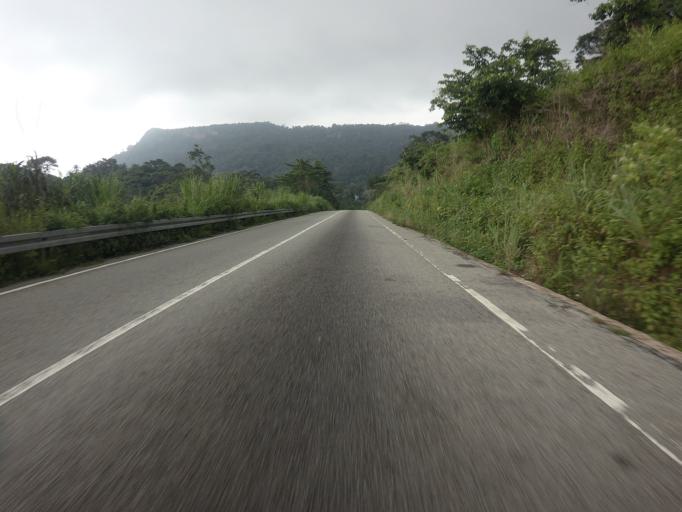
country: GH
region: Volta
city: Kpandu
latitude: 6.8176
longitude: 0.4232
